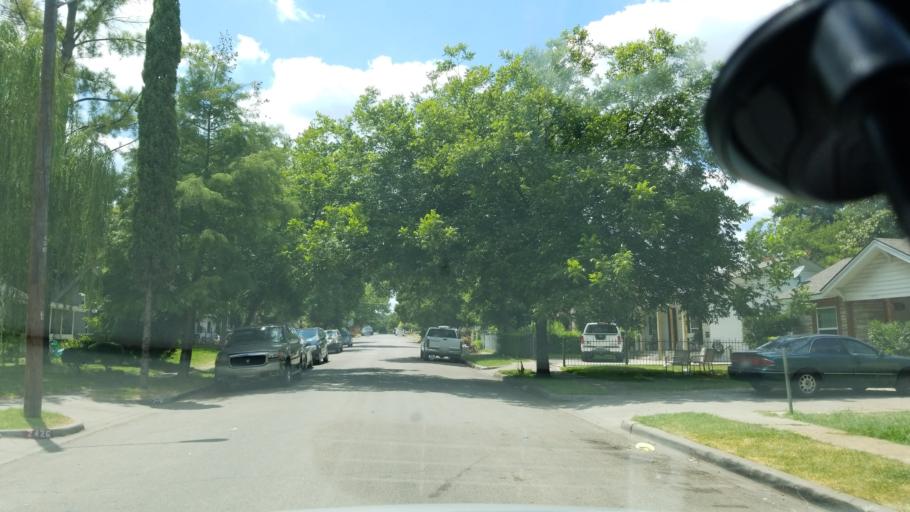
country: US
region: Texas
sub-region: Dallas County
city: Cockrell Hill
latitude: 32.7302
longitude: -96.8580
